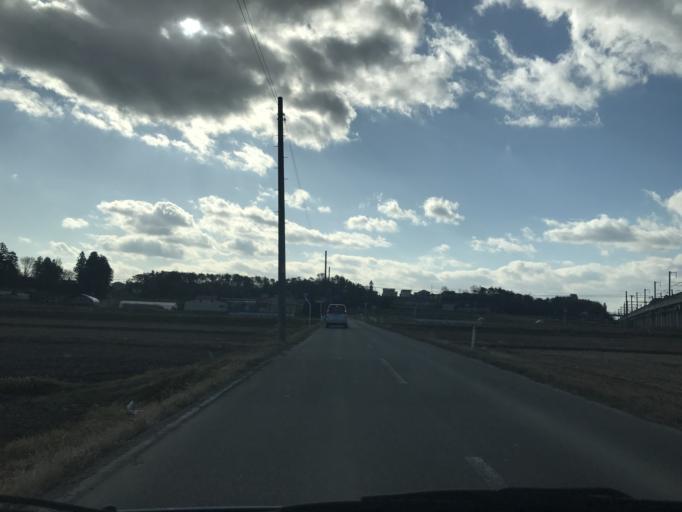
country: JP
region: Miyagi
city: Kogota
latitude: 38.7389
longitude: 141.0664
